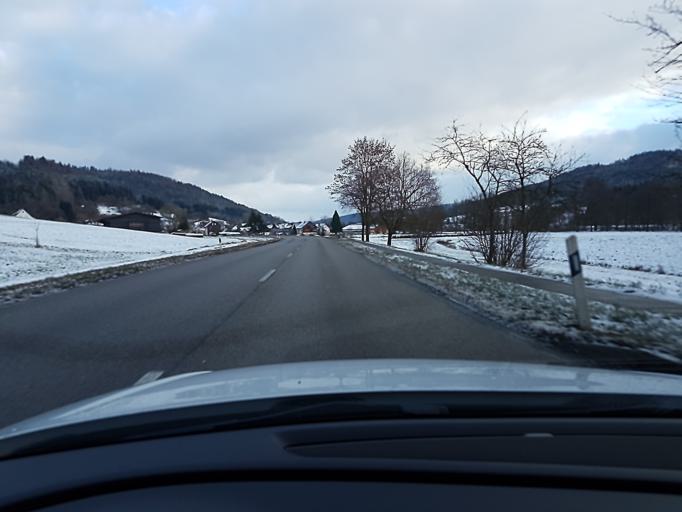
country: DE
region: Baden-Wuerttemberg
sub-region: Regierungsbezirk Stuttgart
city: Sulzbach an der Murr
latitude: 48.9983
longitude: 9.5259
